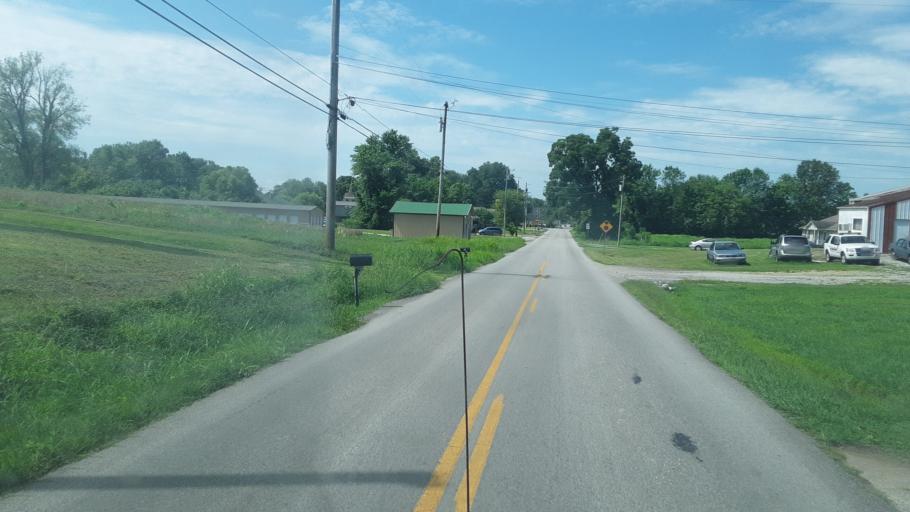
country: US
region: Kentucky
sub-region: Christian County
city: Oak Grove
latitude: 36.7804
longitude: -87.3519
